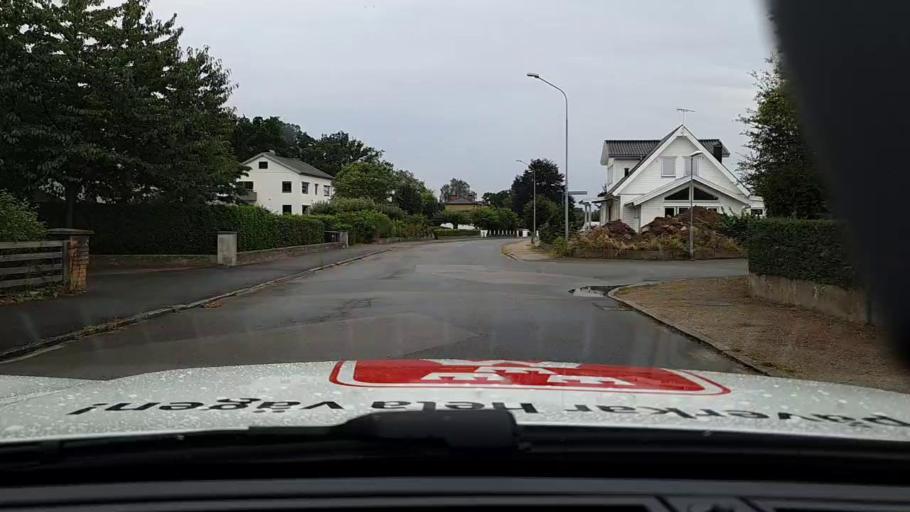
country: SE
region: Skane
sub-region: Hassleholms Kommun
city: Hassleholm
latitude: 56.1676
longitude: 13.7740
